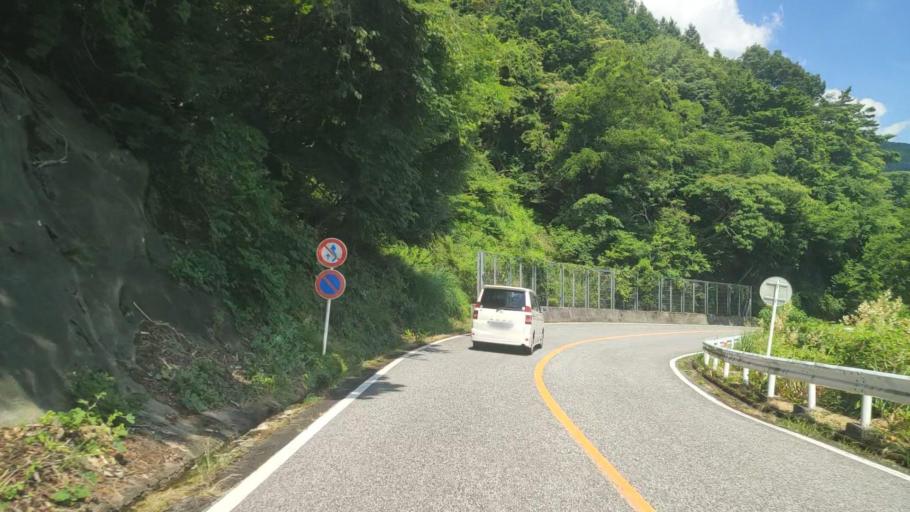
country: JP
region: Gifu
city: Tarui
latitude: 35.3918
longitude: 136.4329
